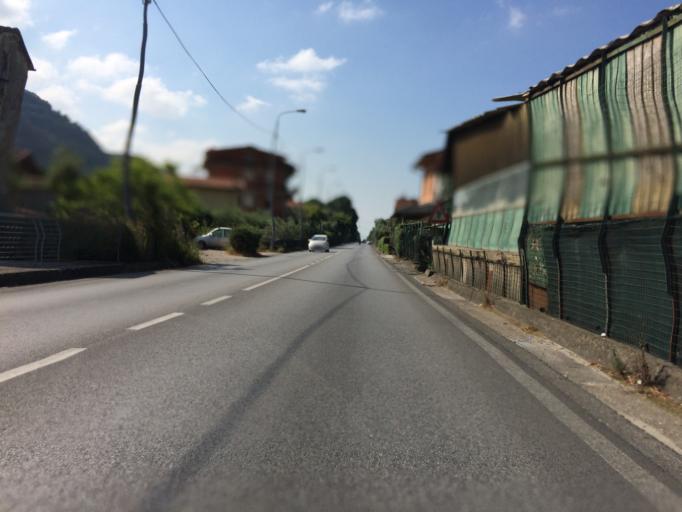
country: IT
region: Tuscany
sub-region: Provincia di Massa-Carrara
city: Capanne-Prato-Cinquale
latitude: 44.0142
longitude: 10.1571
